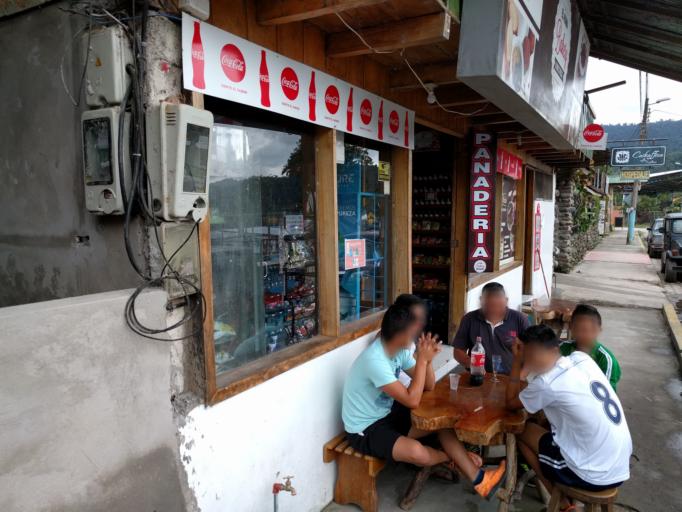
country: EC
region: Pichincha
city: Quito
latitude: -0.0527
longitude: -78.7757
